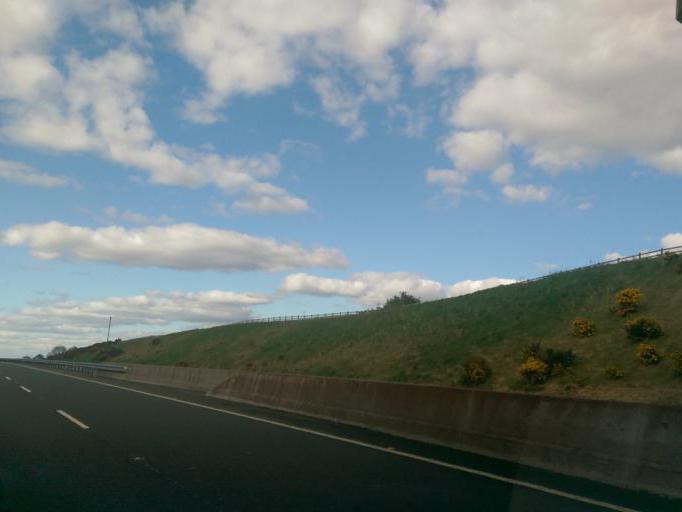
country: IE
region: Leinster
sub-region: An Iarmhi
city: Athlone
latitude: 53.3826
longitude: -8.0509
